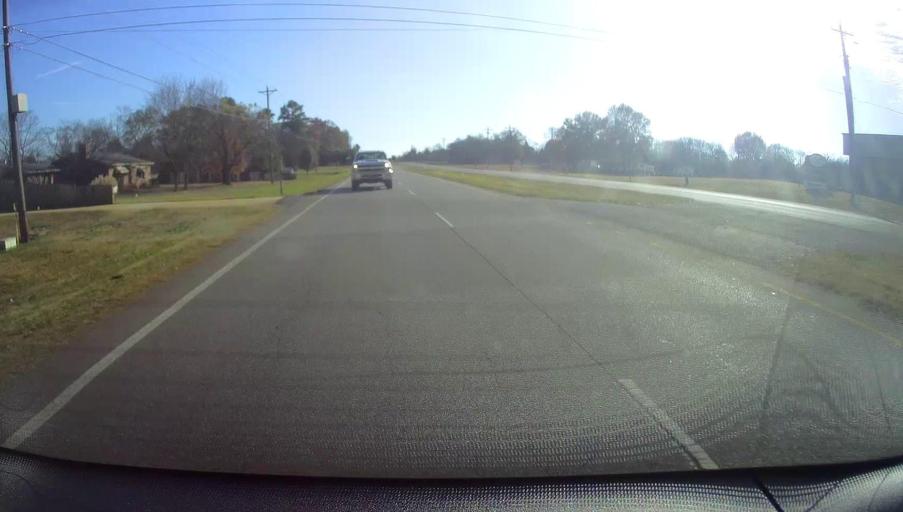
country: US
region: Alabama
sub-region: Limestone County
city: Athens
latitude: 34.7531
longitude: -86.9570
